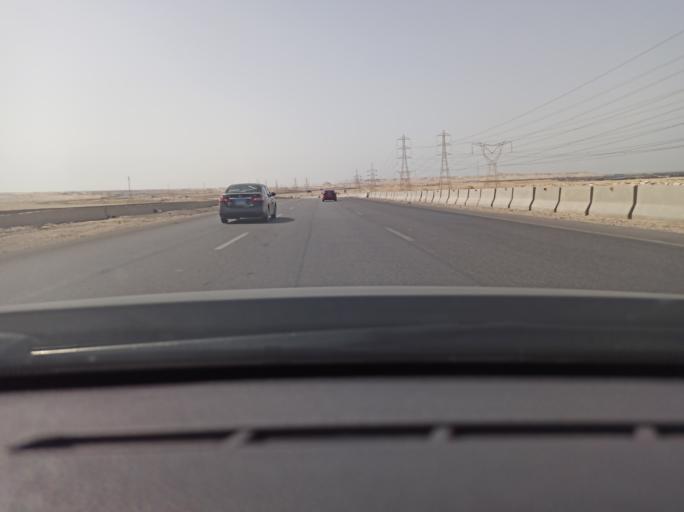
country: EG
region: Muhafazat al Qahirah
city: Halwan
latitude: 29.7302
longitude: 31.4065
